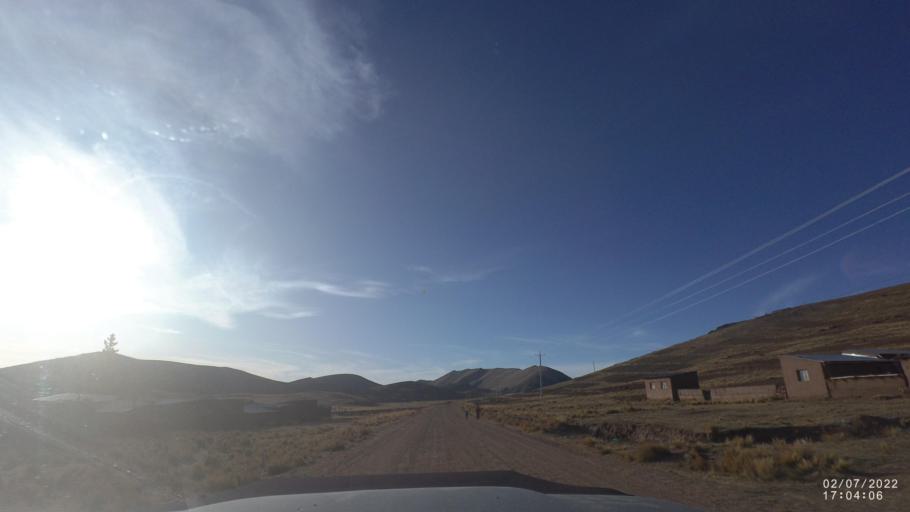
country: BO
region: Cochabamba
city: Irpa Irpa
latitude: -17.9183
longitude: -66.5580
